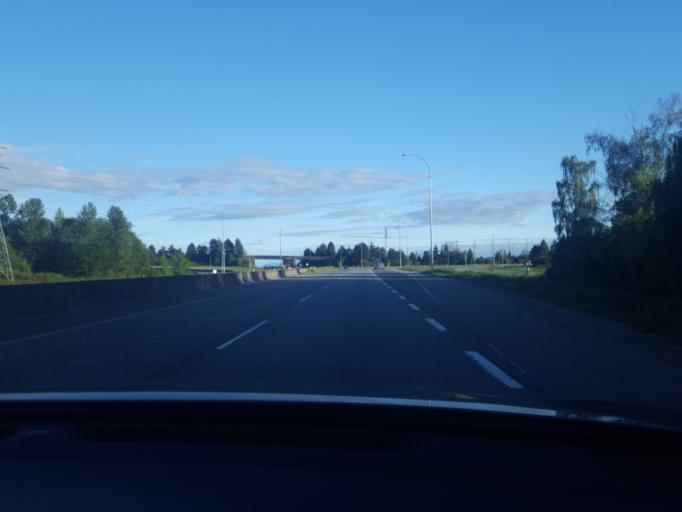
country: CA
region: British Columbia
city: Delta
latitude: 49.1237
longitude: -122.9279
